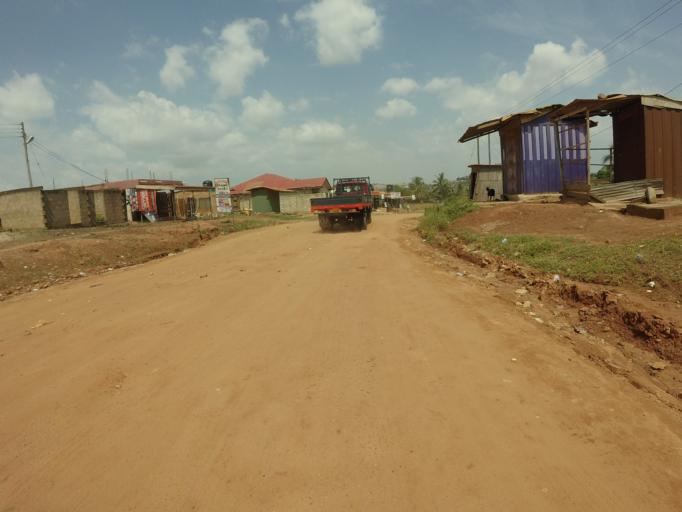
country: GH
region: Greater Accra
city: Gbawe
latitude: 5.6191
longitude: -0.3088
